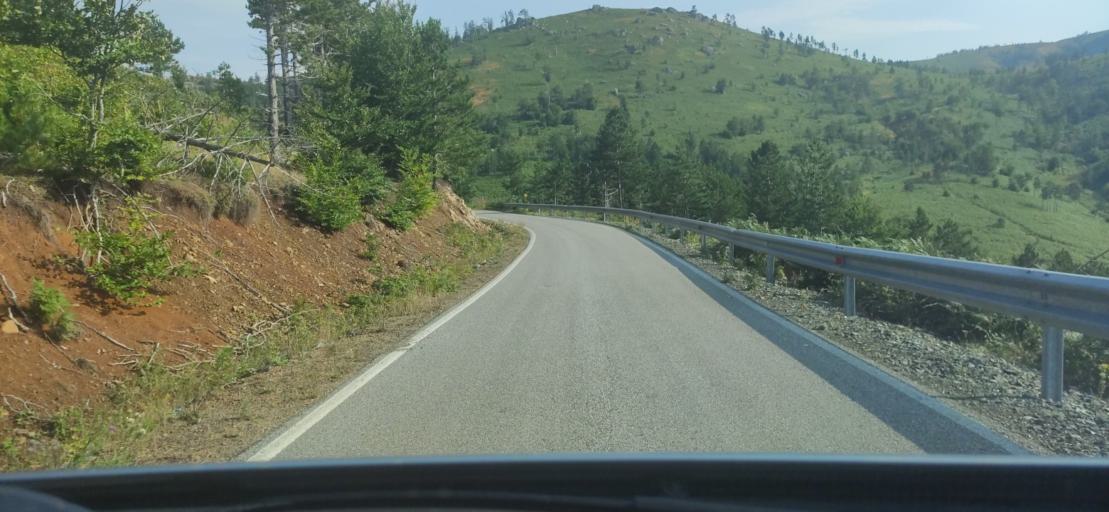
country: AL
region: Shkoder
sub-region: Rrethi i Pukes
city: Iballe
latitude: 42.1736
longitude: 20.0256
